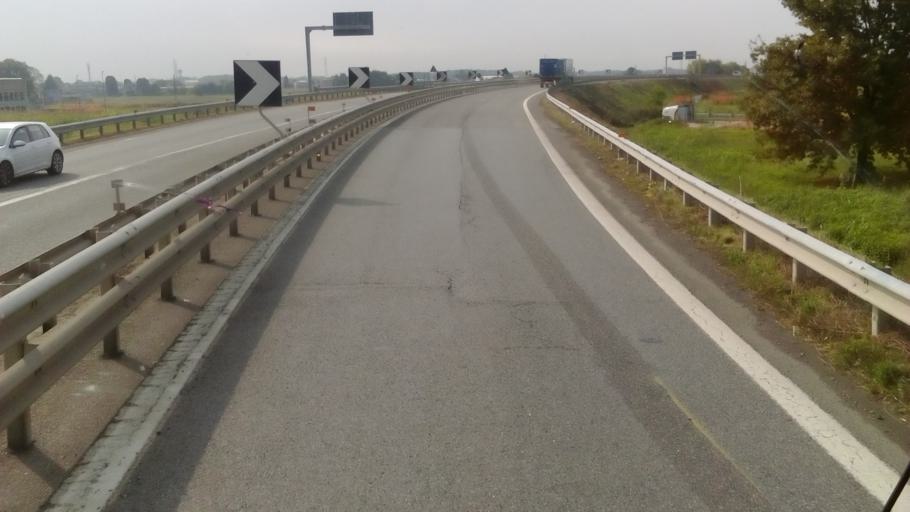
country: IT
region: Lombardy
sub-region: Provincia di Como
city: Carimate
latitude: 45.6942
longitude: 9.0987
